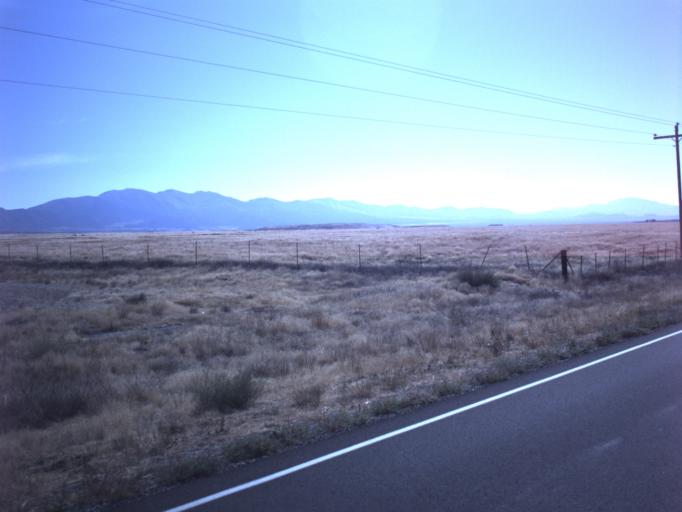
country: US
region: Utah
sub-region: Tooele County
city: Grantsville
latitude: 40.3815
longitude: -112.7470
